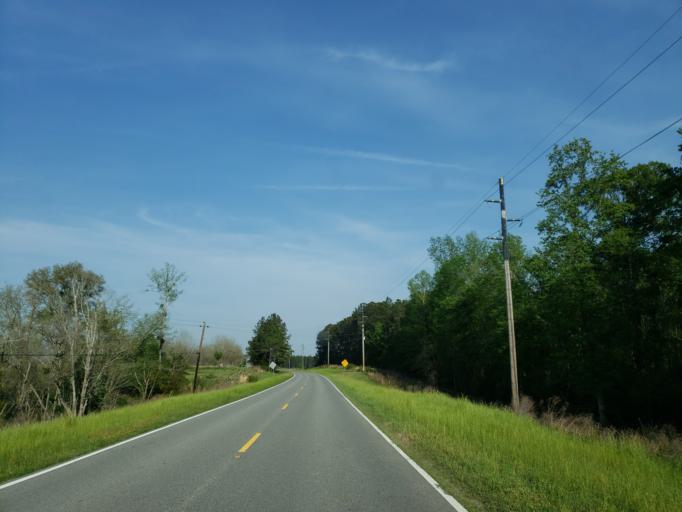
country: US
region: Georgia
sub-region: Tift County
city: Tifton
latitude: 31.5714
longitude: -83.5296
